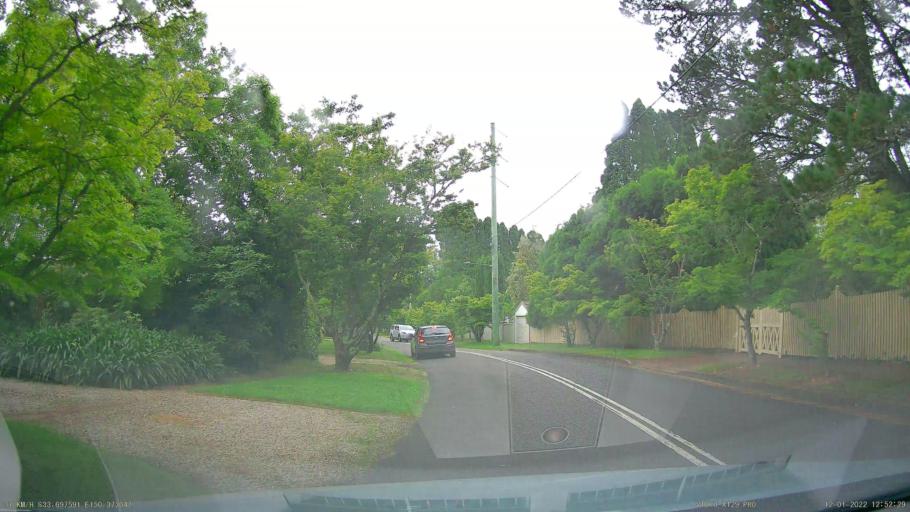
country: AU
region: New South Wales
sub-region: Blue Mountains Municipality
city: Leura
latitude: -33.6974
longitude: 150.3730
